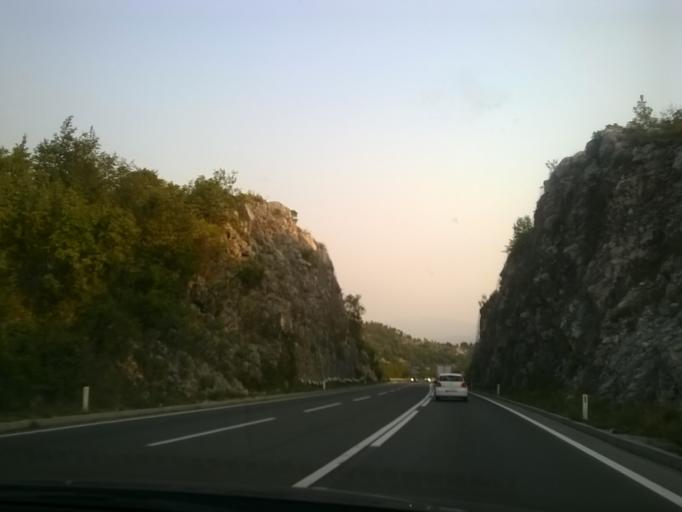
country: ME
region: Opstina Niksic
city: Niksic
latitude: 42.7009
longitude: 18.9609
